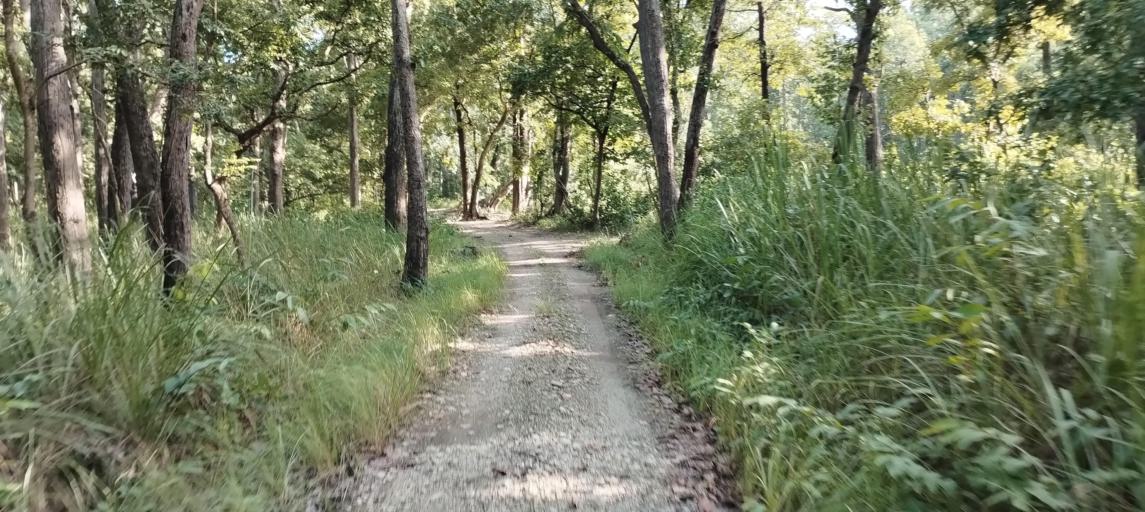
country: NP
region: Far Western
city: Tikapur
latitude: 28.5320
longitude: 81.2834
